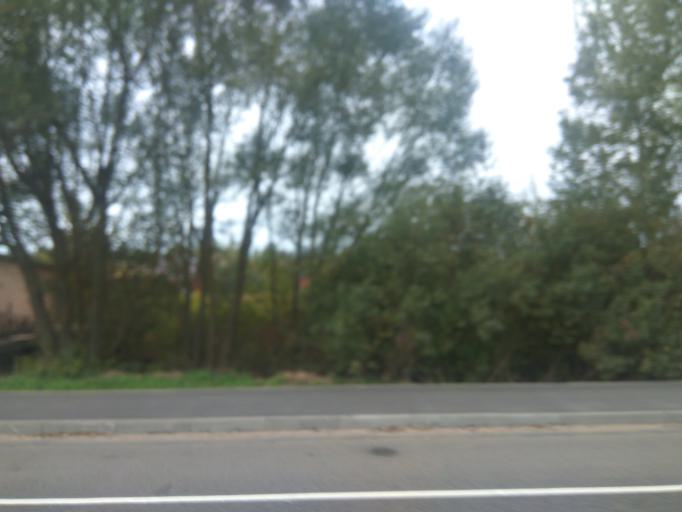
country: RU
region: Moskovskaya
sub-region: Shchelkovskiy Rayon
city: Grebnevo
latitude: 55.9972
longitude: 38.1282
